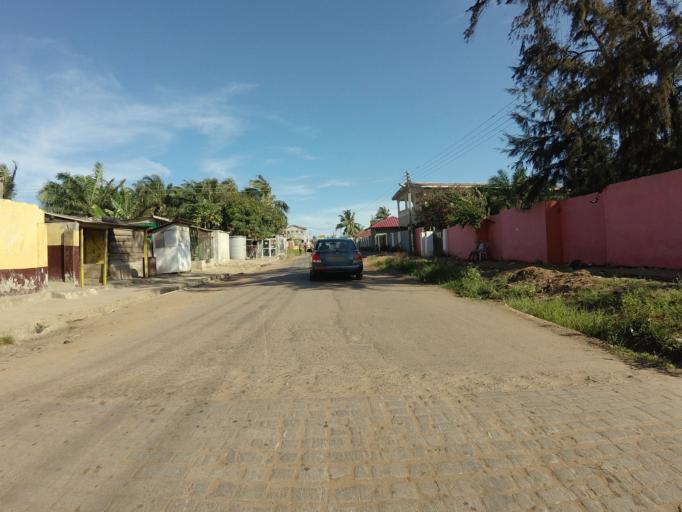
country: GH
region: Greater Accra
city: Nungua
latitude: 5.5919
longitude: -0.0831
